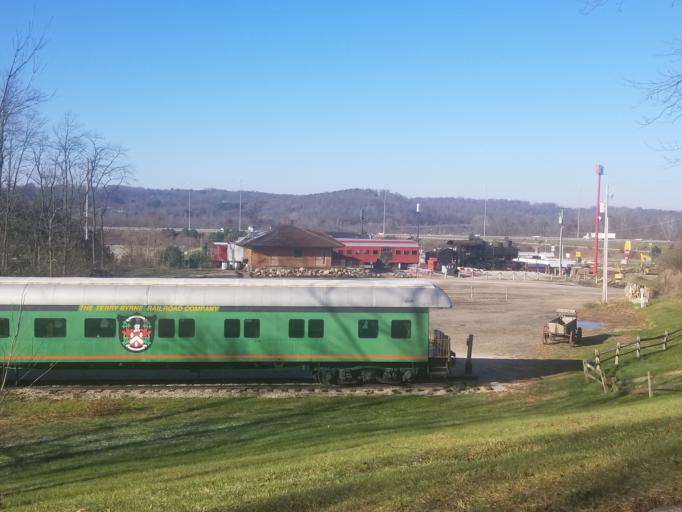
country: US
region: Ohio
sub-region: Richland County
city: Lexington
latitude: 40.6776
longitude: -82.5647
